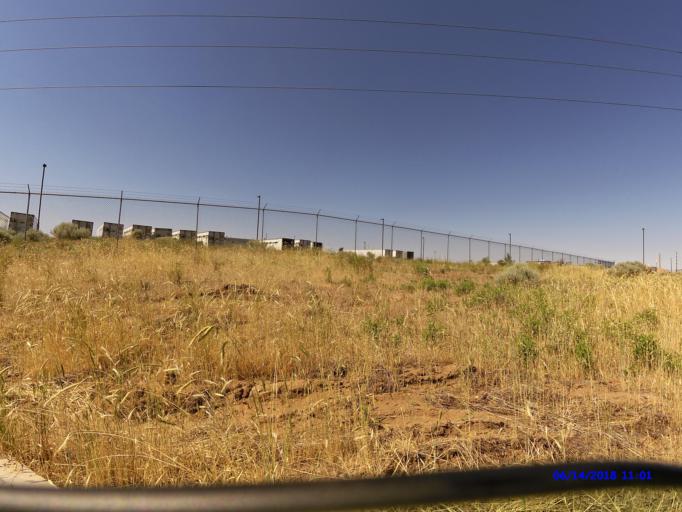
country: US
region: Utah
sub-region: Weber County
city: Ogden
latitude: 41.2096
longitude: -111.9997
